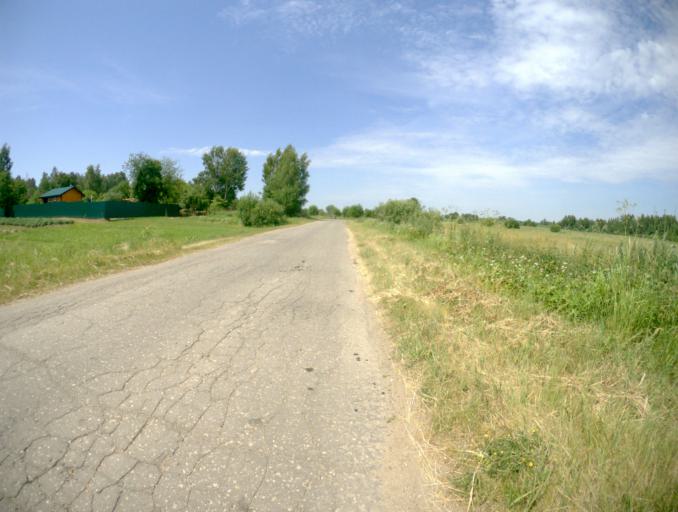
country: RU
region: Vladimir
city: Vorsha
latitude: 56.0237
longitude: 40.1911
